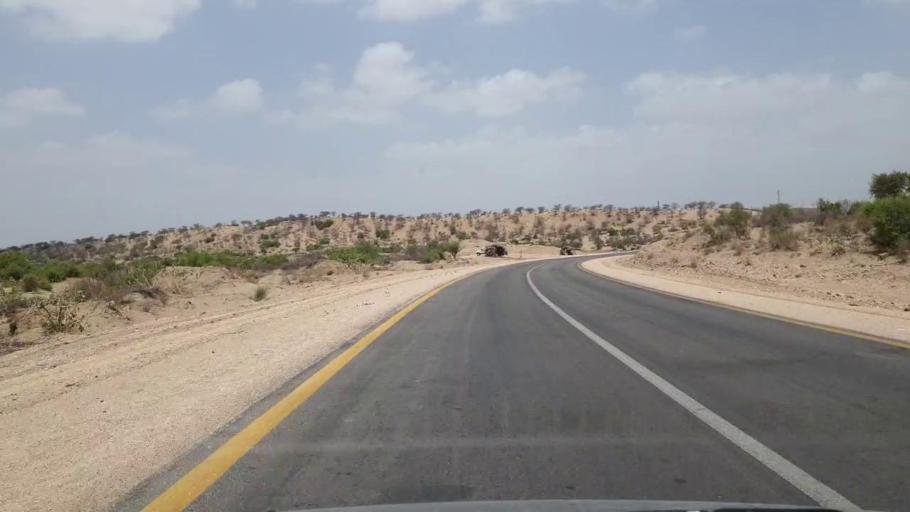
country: PK
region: Sindh
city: Mithi
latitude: 24.8284
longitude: 69.6185
